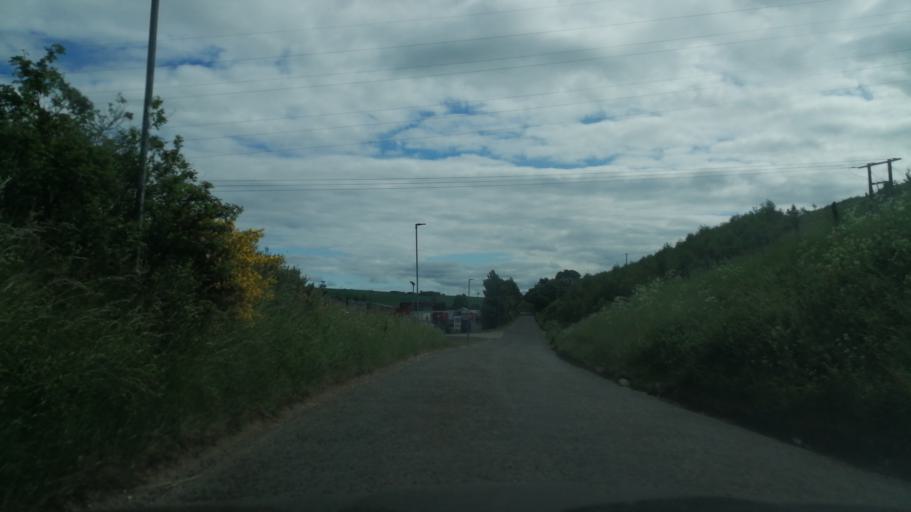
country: GB
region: Scotland
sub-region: Moray
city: Keith
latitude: 57.5512
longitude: -2.9510
